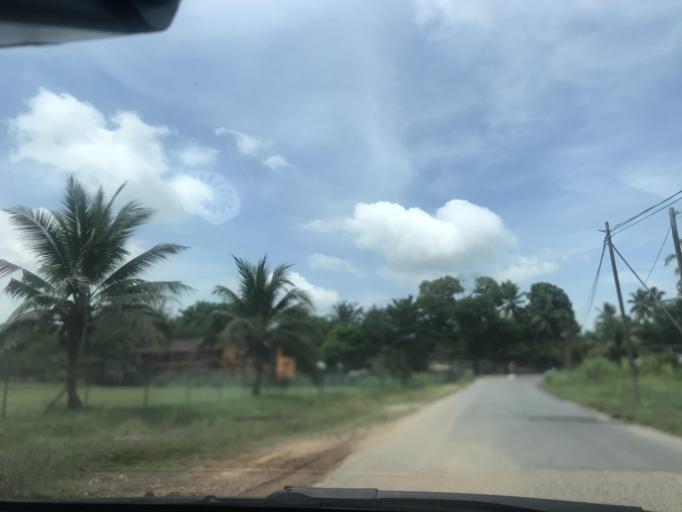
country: MY
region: Kelantan
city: Tumpat
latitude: 6.2192
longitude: 102.1191
